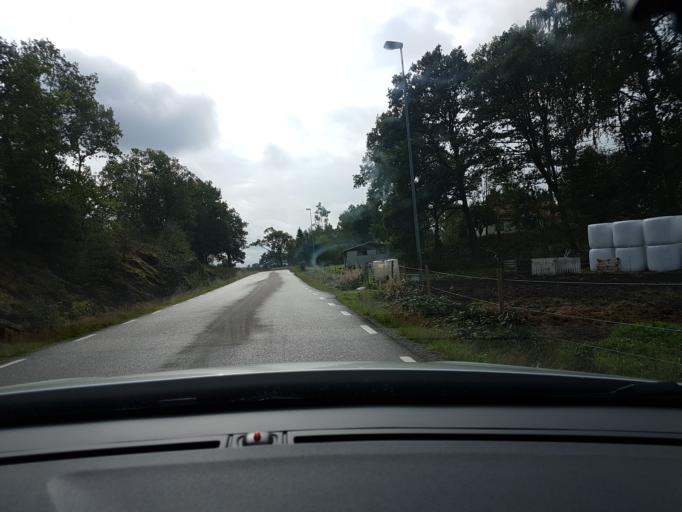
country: SE
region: Vaestra Goetaland
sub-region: Ale Kommun
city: Alvangen
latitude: 57.9150
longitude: 12.1446
